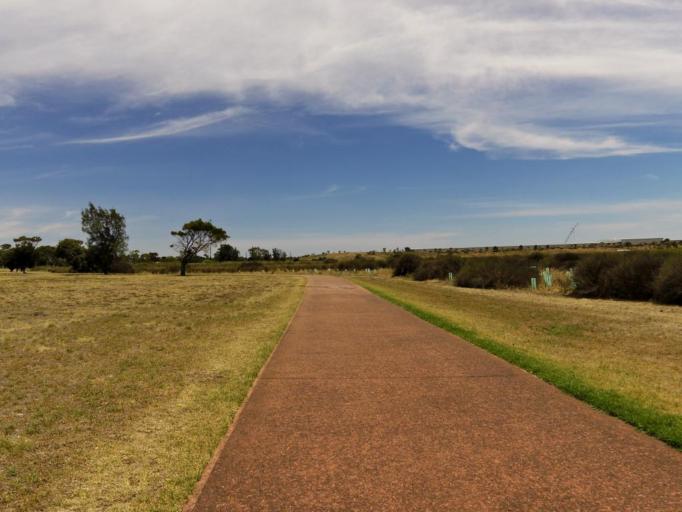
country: AU
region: Victoria
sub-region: Hobsons Bay
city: Altona
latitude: -37.8598
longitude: 144.8303
